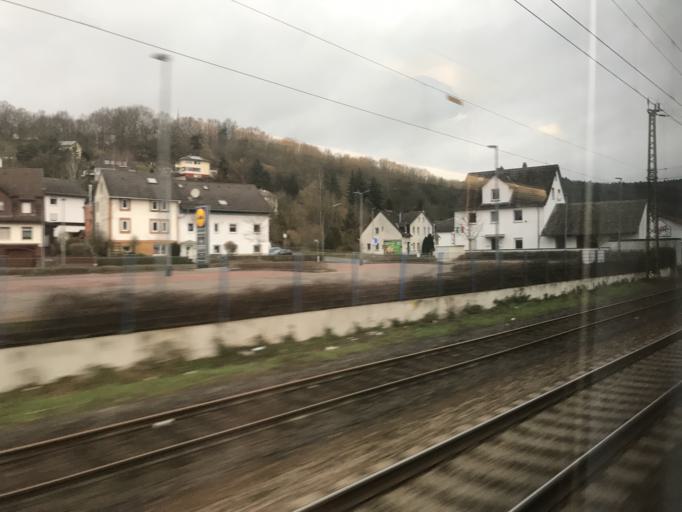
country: DE
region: Hesse
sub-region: Regierungsbezirk Kassel
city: Bad Hersfeld
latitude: 50.8782
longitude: 9.7225
